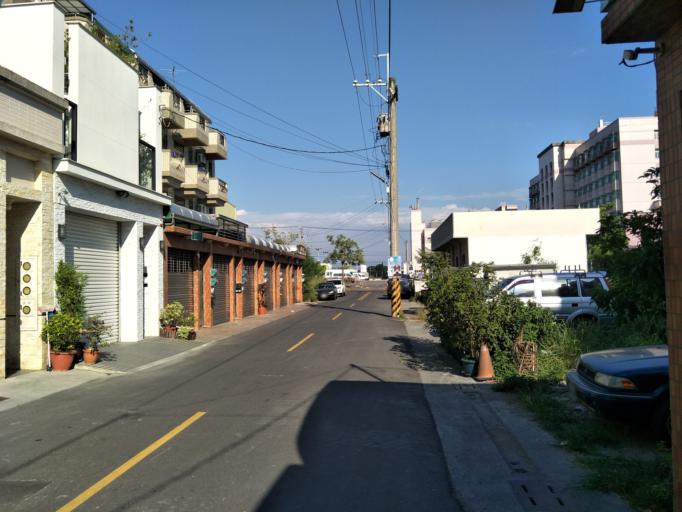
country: TW
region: Taiwan
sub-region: Changhua
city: Chang-hua
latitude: 23.9517
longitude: 120.5255
